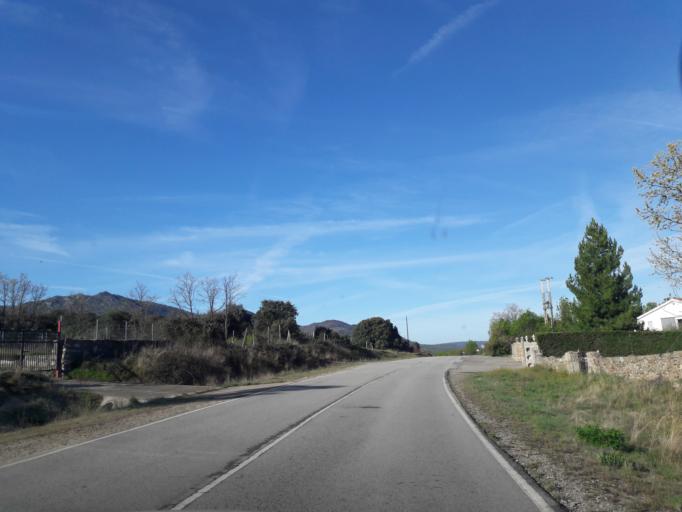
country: ES
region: Castille and Leon
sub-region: Provincia de Salamanca
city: Ledrada
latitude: 40.4613
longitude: -5.7253
